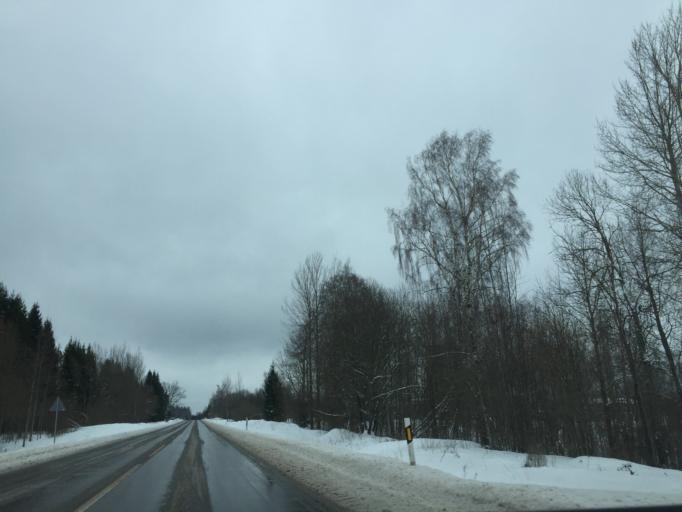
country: LV
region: Ligatne
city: Ligatne
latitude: 57.1759
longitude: 25.0404
